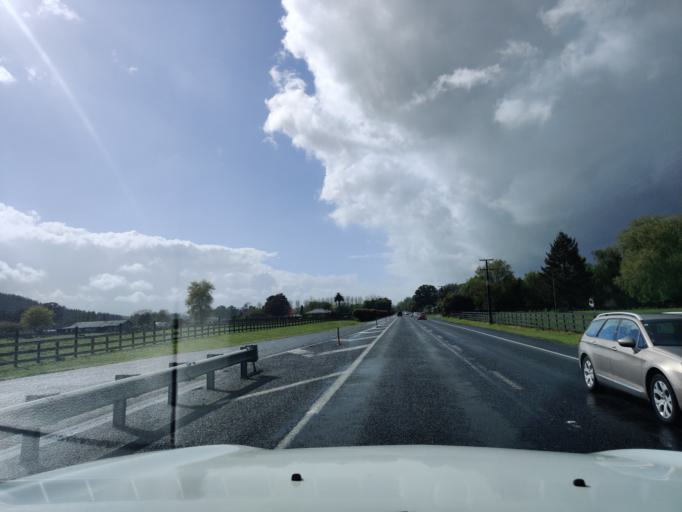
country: NZ
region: Waikato
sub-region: Waipa District
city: Cambridge
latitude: -37.9091
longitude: 175.5323
